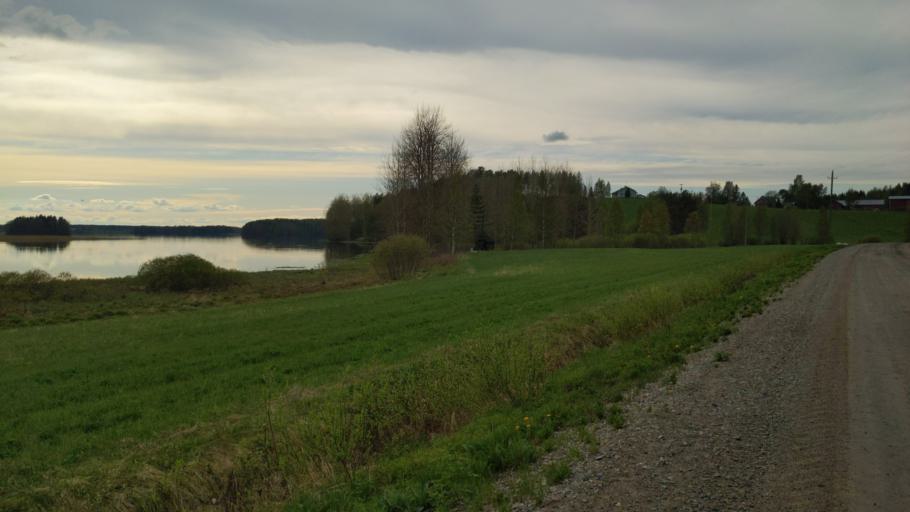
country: FI
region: Northern Savo
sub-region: Ylae-Savo
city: Vieremae
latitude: 63.5886
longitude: 26.9819
